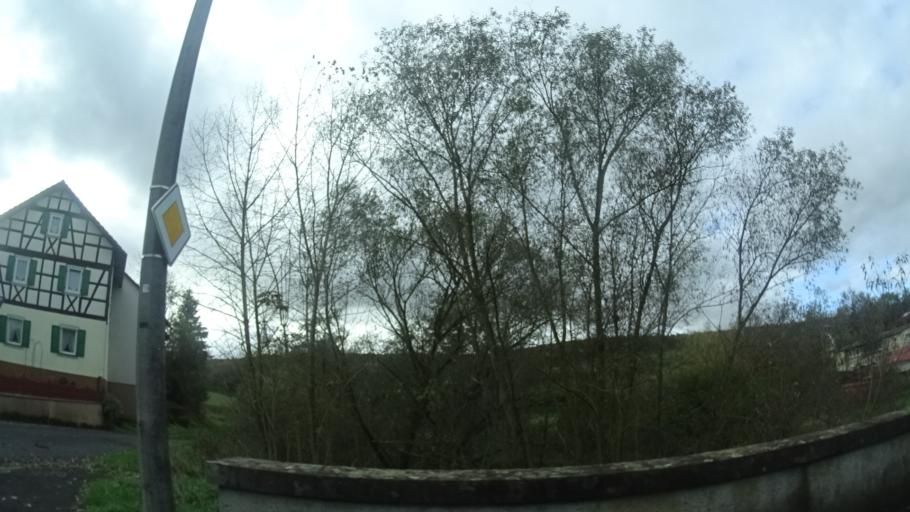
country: DE
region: Bavaria
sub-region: Regierungsbezirk Unterfranken
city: Aubstadt
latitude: 50.3562
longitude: 10.4235
